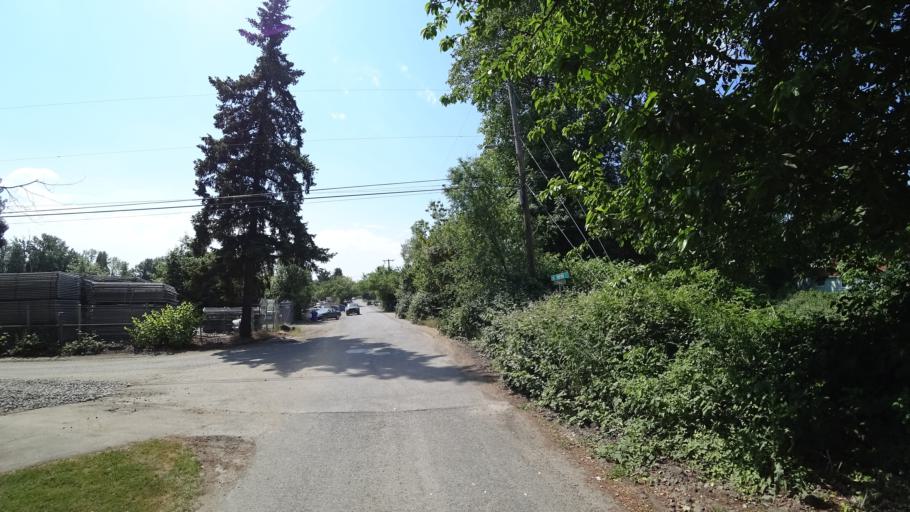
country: US
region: Oregon
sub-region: Multnomah County
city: Lents
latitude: 45.5653
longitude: -122.5506
